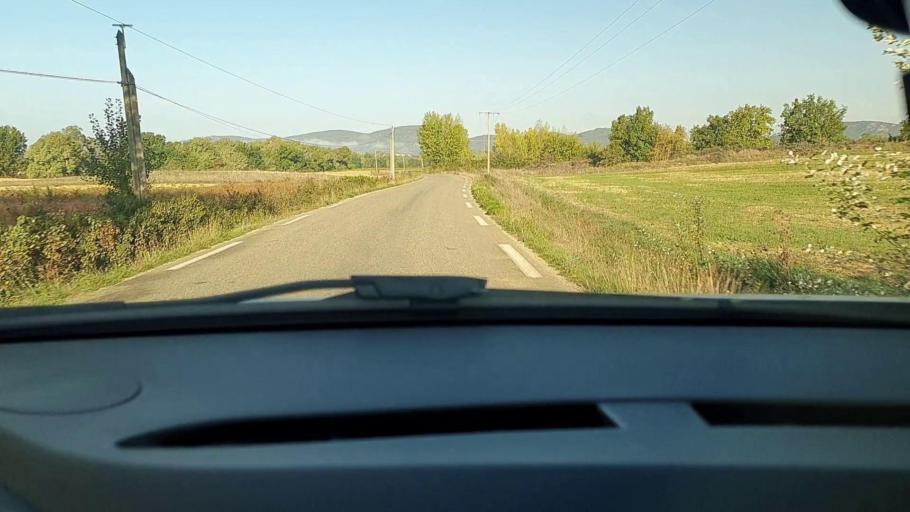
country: FR
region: Languedoc-Roussillon
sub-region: Departement du Gard
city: Barjac
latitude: 44.2618
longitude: 4.2834
